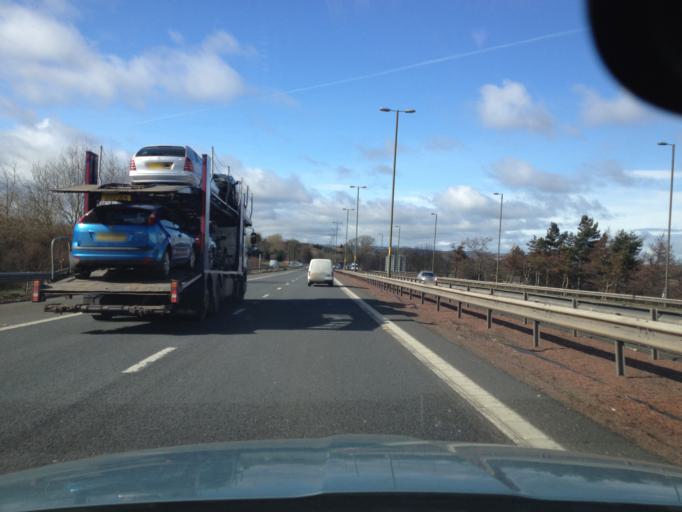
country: GB
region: Scotland
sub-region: Edinburgh
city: Newbridge
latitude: 55.9258
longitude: -3.4122
